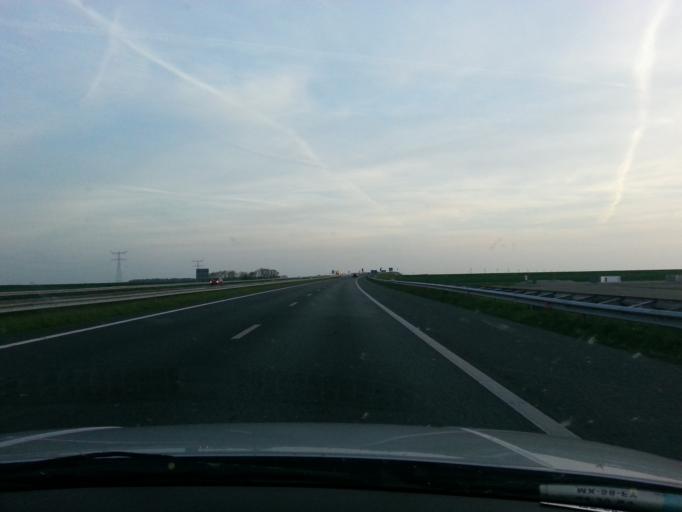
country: NL
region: Flevoland
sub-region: Gemeente Urk
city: Urk
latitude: 52.6218
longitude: 5.6606
